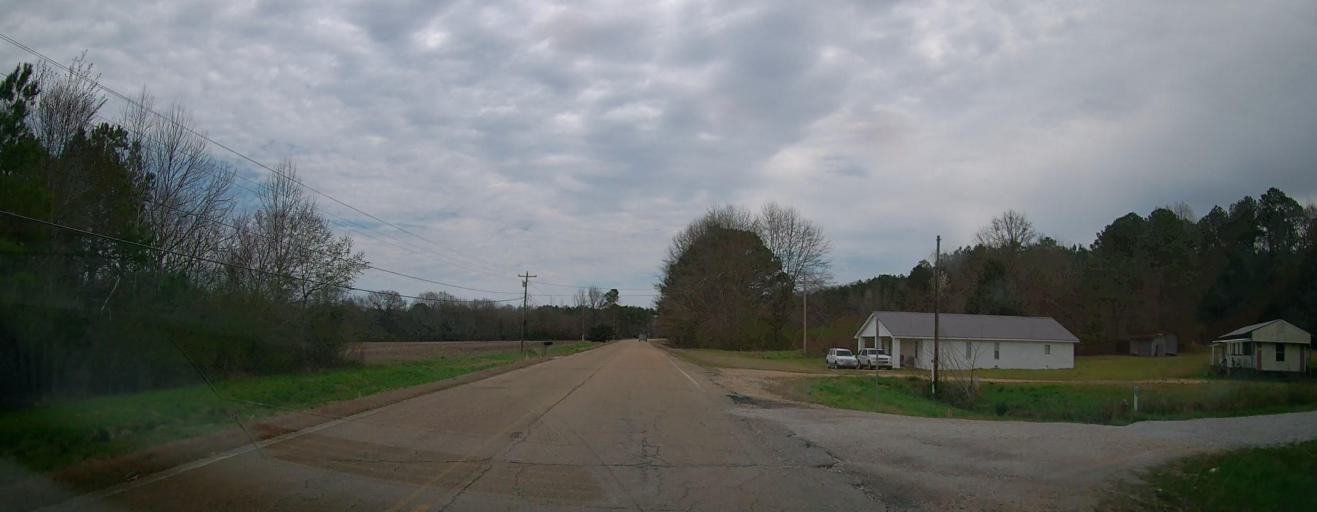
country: US
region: Mississippi
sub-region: Itawamba County
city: Fulton
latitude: 34.2306
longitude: -88.2433
